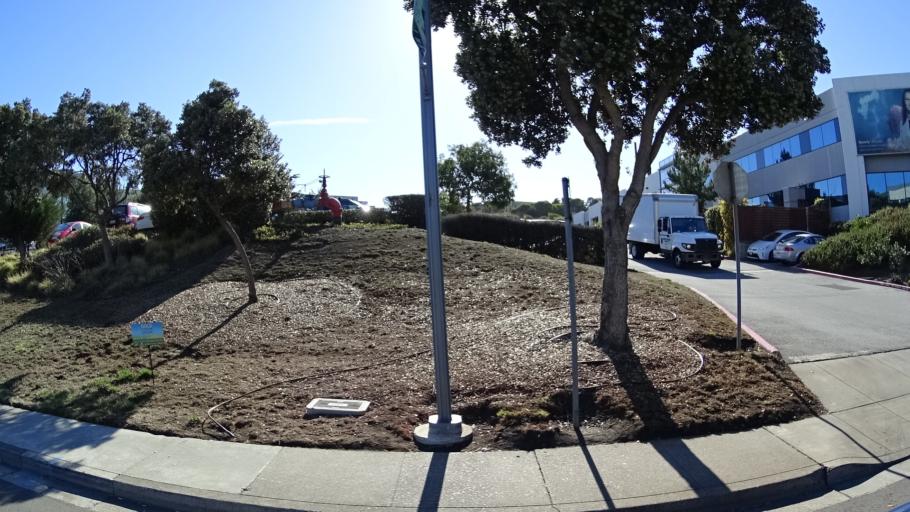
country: US
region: California
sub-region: San Mateo County
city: South San Francisco
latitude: 37.6549
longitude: -122.3834
